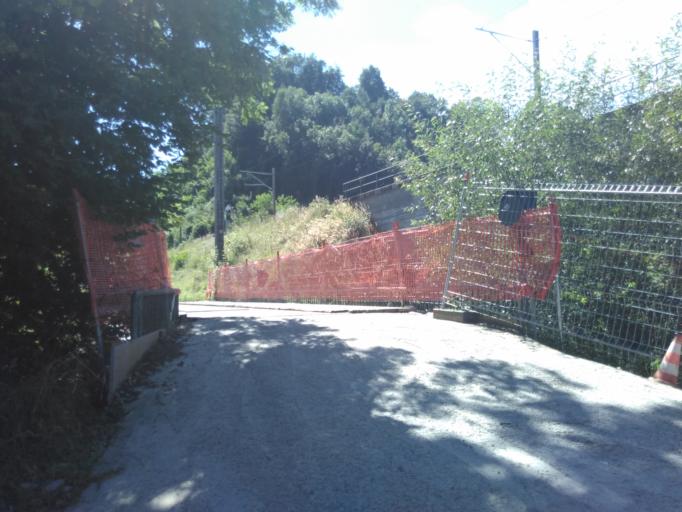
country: CH
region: Saint Gallen
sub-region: Wahlkreis See-Gaster
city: Jona
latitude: 47.2367
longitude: 8.8375
